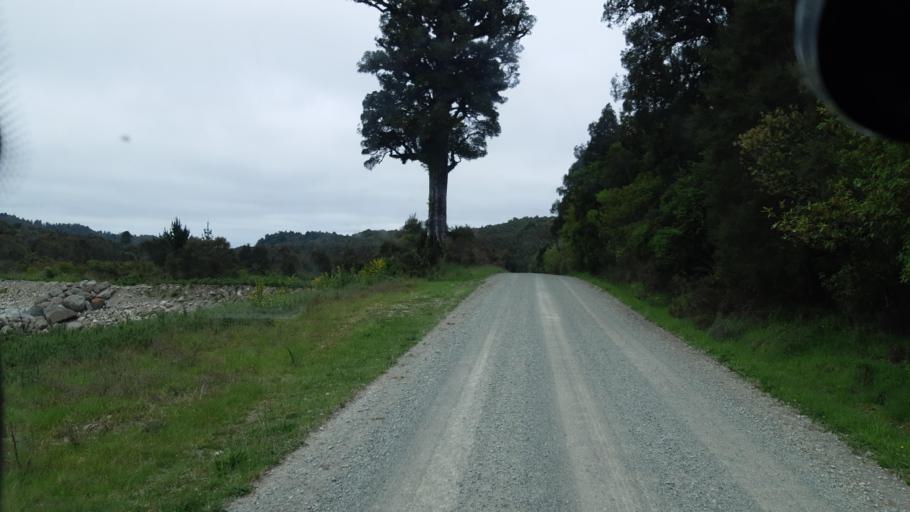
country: NZ
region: West Coast
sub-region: Grey District
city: Greymouth
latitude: -42.6362
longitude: 171.2882
